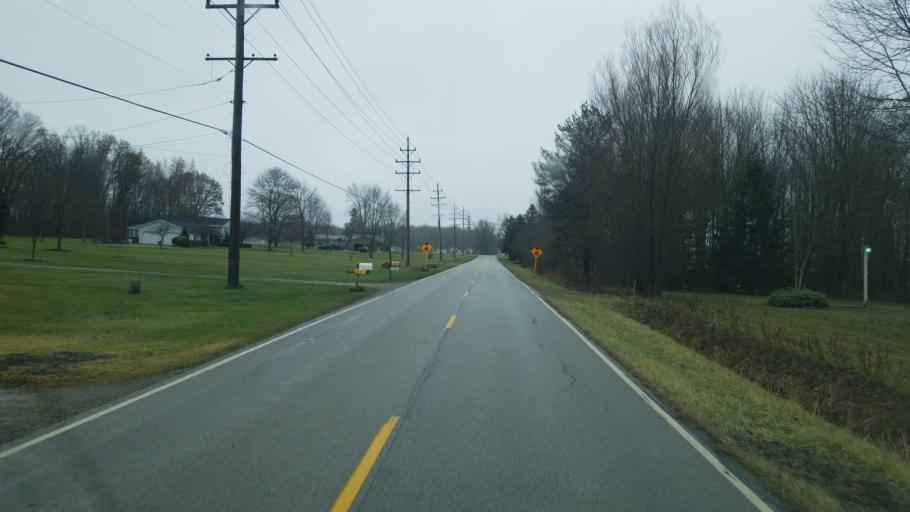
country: US
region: Ohio
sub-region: Ashtabula County
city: Jefferson
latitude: 41.7639
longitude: -80.8099
